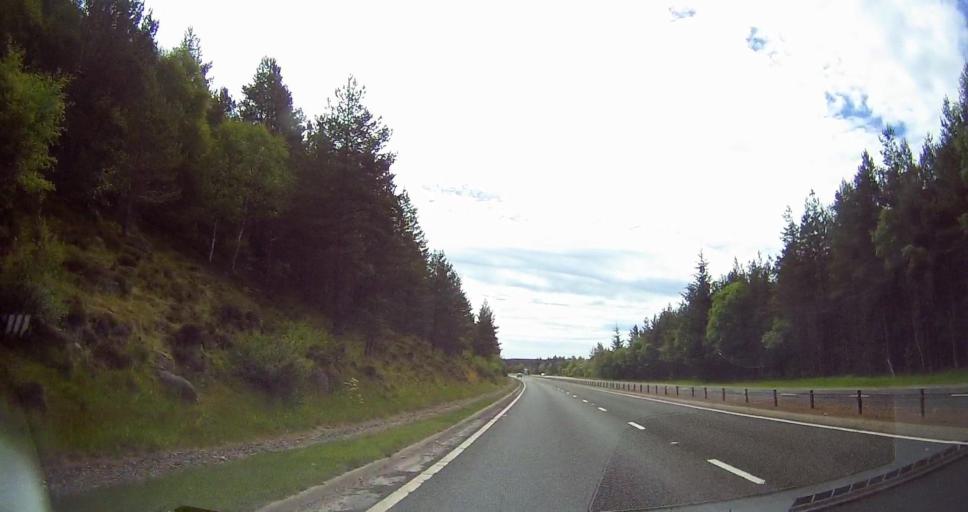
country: GB
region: Scotland
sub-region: Highland
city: Aviemore
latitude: 57.3201
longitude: -3.9723
